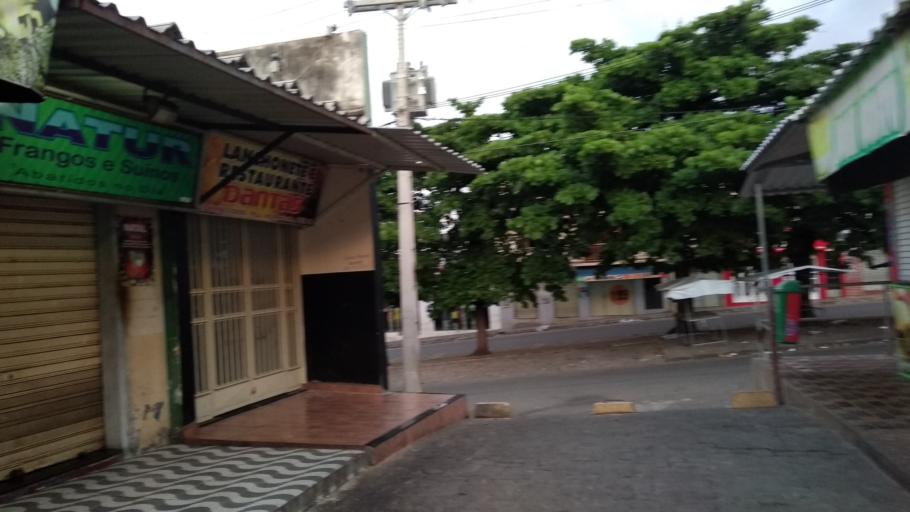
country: BR
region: Bahia
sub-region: Caetite
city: Caetite
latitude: -14.0661
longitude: -42.4905
